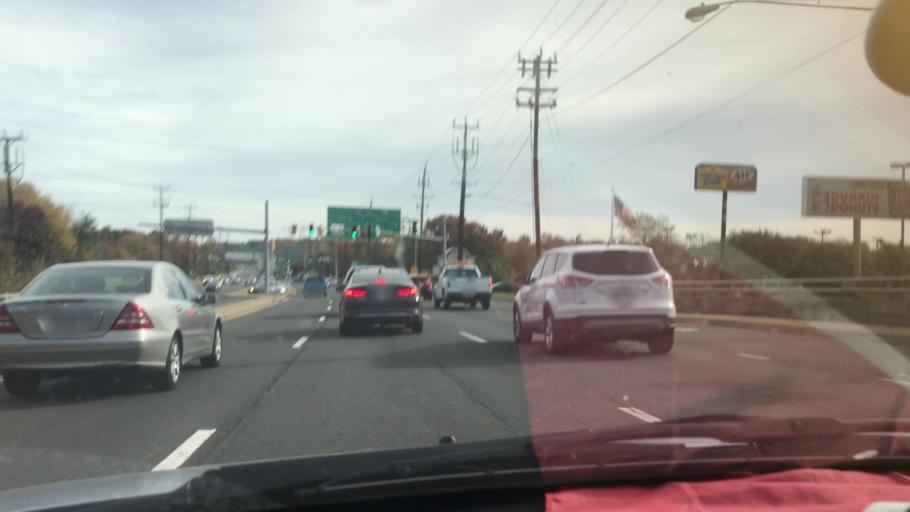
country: US
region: Maryland
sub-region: Prince George's County
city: Largo
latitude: 38.8908
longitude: -76.8516
